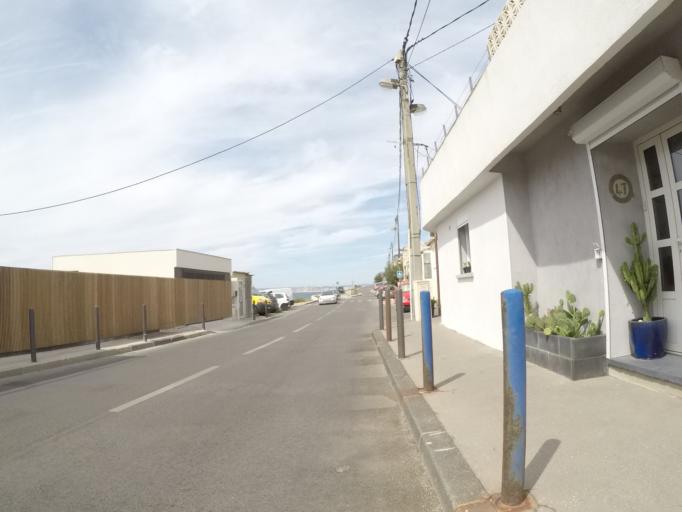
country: FR
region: Provence-Alpes-Cote d'Azur
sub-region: Departement des Bouches-du-Rhone
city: Marseille 08
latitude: 43.2178
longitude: 5.3460
